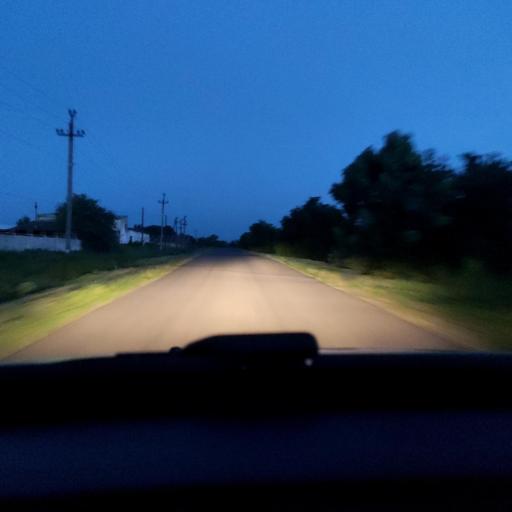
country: RU
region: Voronezj
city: Panino
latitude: 51.6426
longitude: 40.1268
